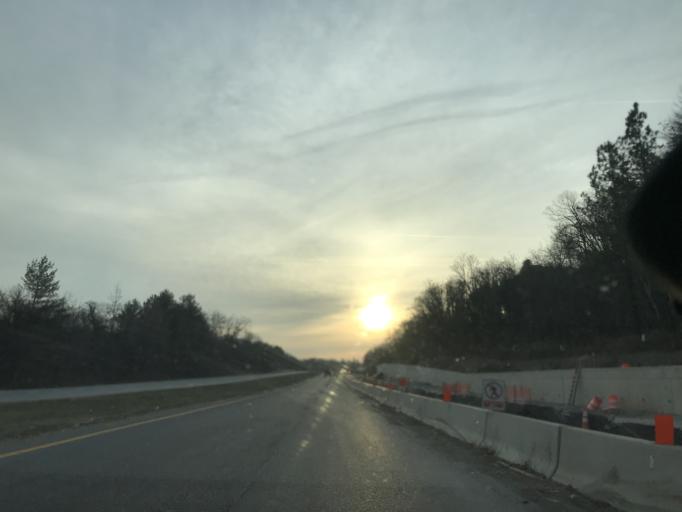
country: US
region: Maryland
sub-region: Prince George's County
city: Woodlawn
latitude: 38.9629
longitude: -76.9000
